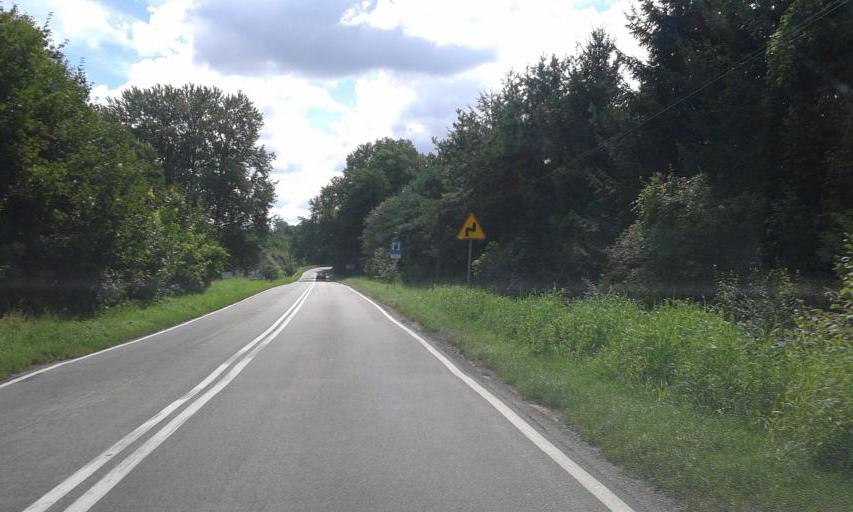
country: PL
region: West Pomeranian Voivodeship
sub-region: Powiat drawski
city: Czaplinek
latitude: 53.5461
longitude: 16.2459
